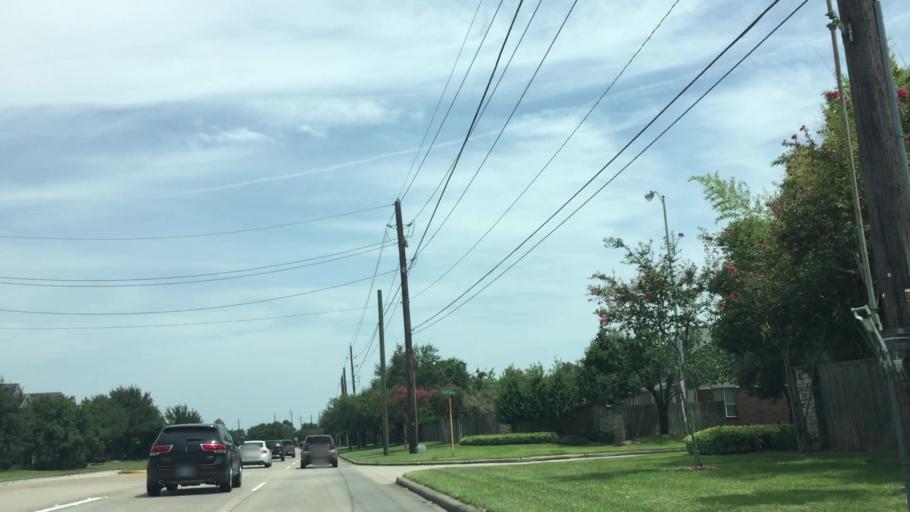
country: US
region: Texas
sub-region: Harris County
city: Jersey Village
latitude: 29.9065
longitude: -95.5614
